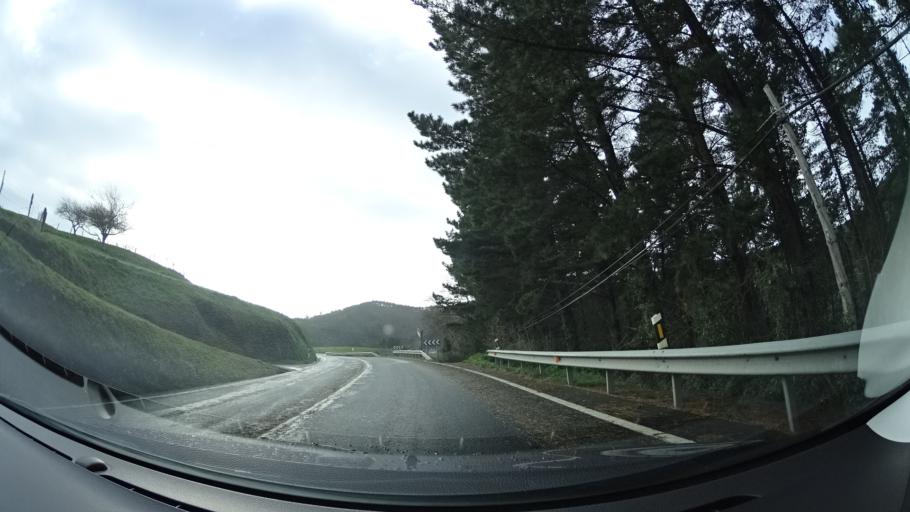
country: ES
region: Basque Country
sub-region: Bizkaia
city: Bermeo
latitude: 43.4152
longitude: -2.7538
